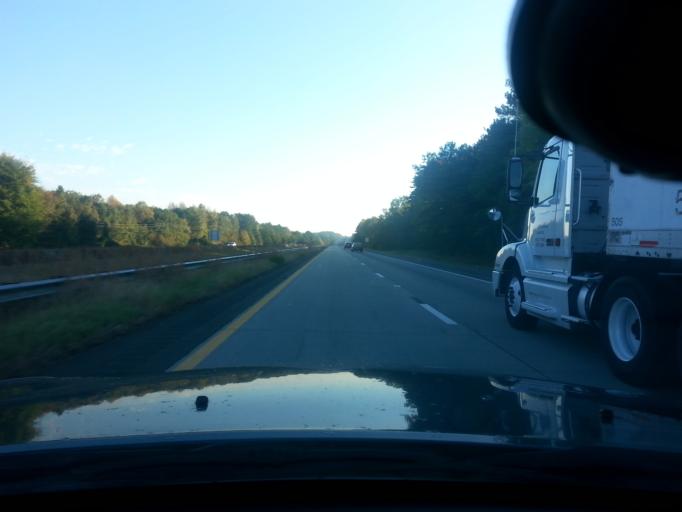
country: US
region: North Carolina
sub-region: Granville County
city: Oxford
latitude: 36.3008
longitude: -78.5708
